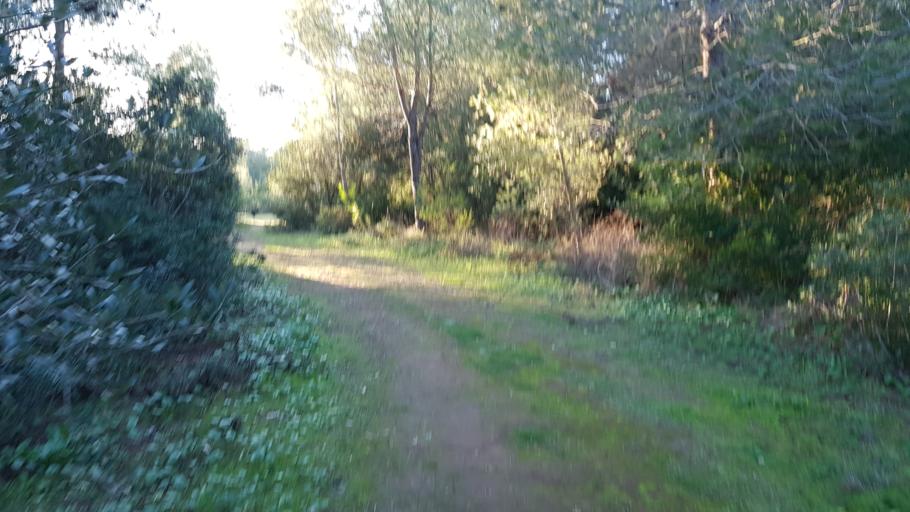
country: IT
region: Apulia
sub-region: Provincia di Lecce
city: Nardo
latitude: 40.1492
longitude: 17.9692
